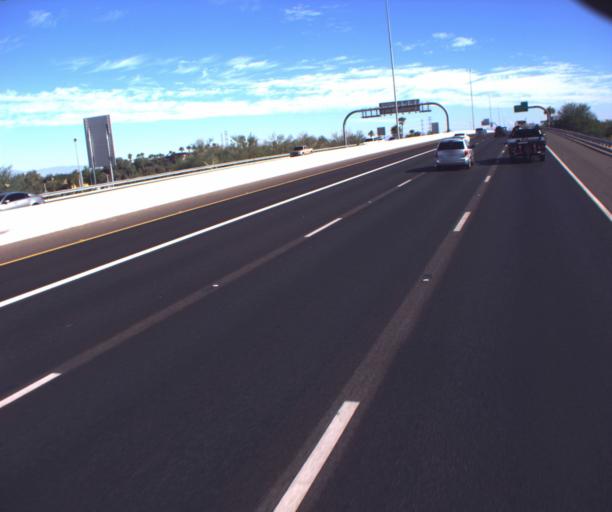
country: US
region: Arizona
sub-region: Maricopa County
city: Peoria
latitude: 33.5495
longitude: -112.2685
